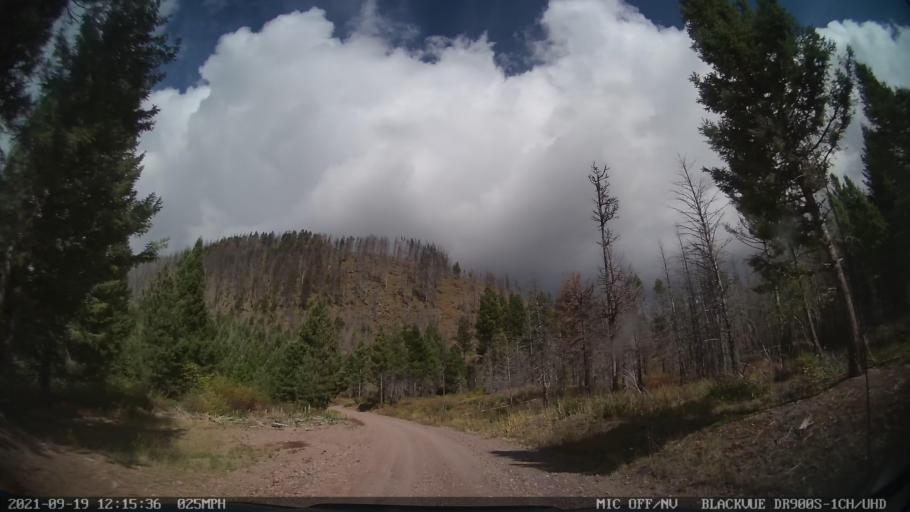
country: US
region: Montana
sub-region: Missoula County
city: Seeley Lake
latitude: 47.1671
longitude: -113.3455
